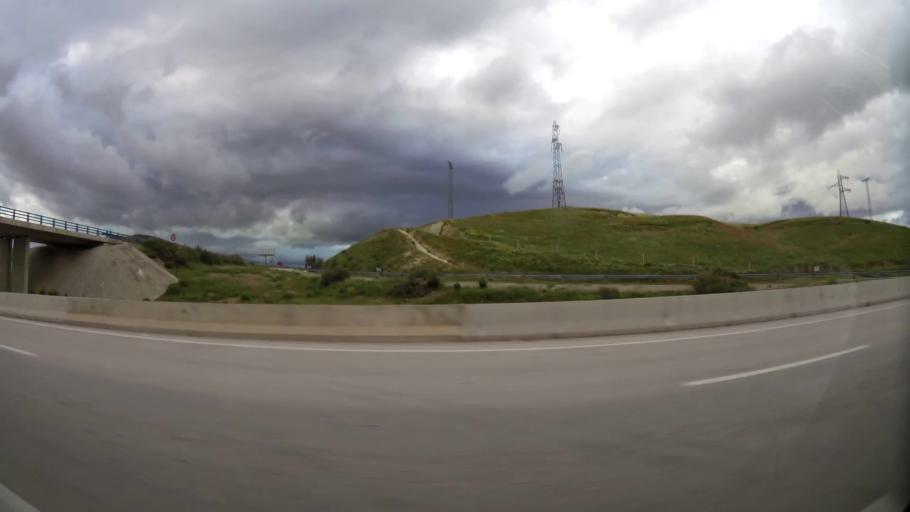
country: MA
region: Taza-Al Hoceima-Taounate
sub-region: Taza
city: Taza
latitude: 34.2605
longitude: -3.9550
